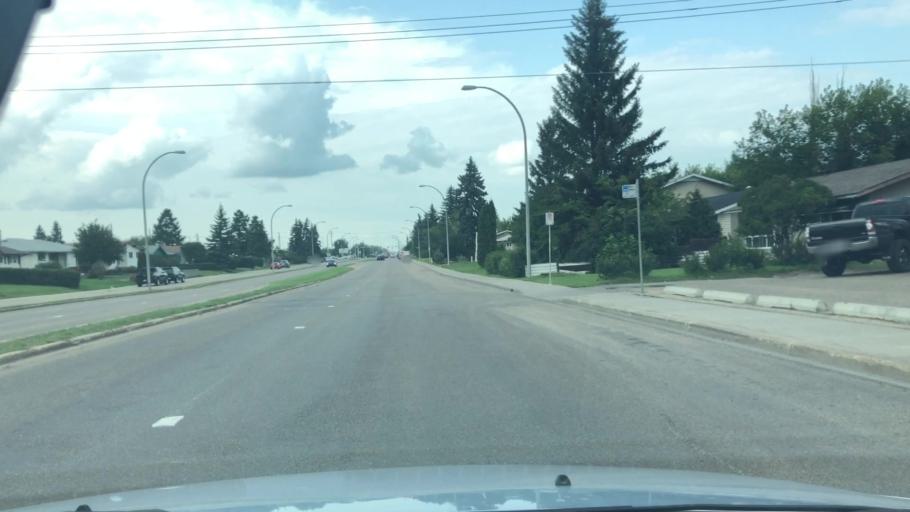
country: CA
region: Alberta
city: Edmonton
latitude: 53.5951
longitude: -113.5166
